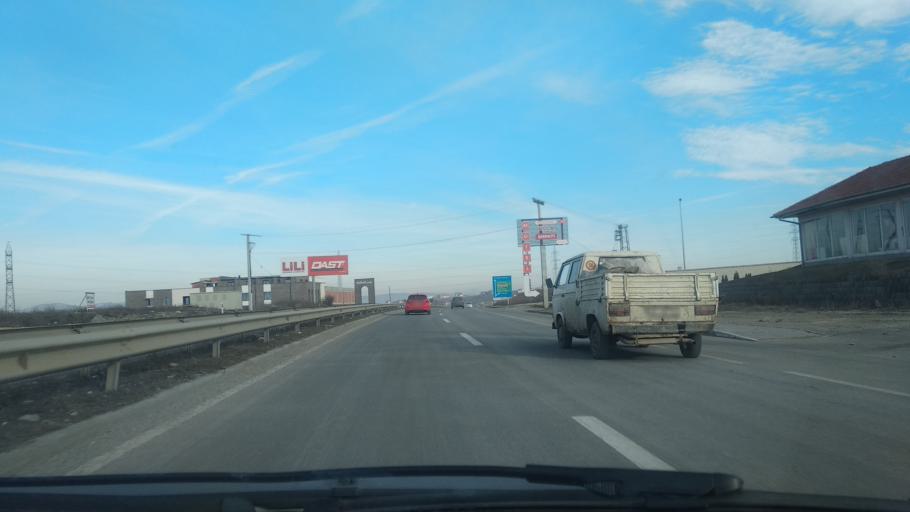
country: XK
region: Pristina
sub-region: Kosovo Polje
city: Kosovo Polje
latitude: 42.6774
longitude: 21.1153
